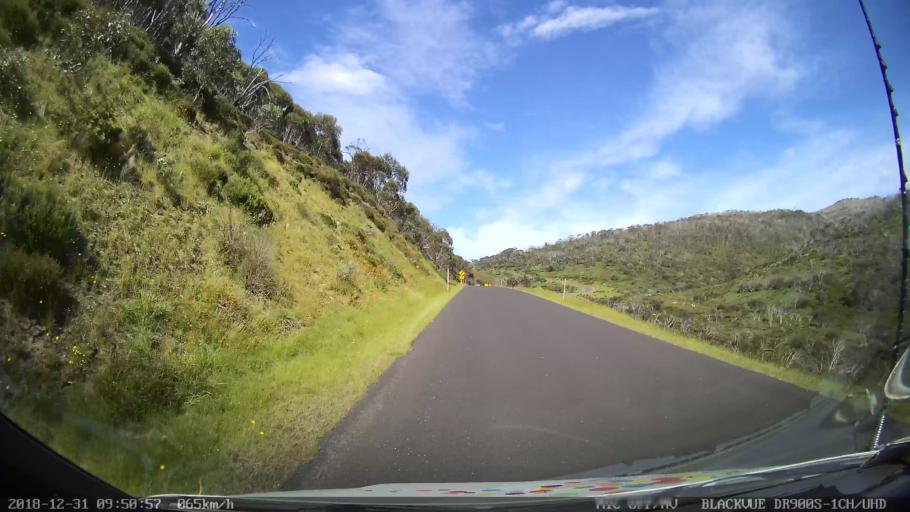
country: AU
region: New South Wales
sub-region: Snowy River
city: Jindabyne
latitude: -36.5224
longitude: 148.2670
